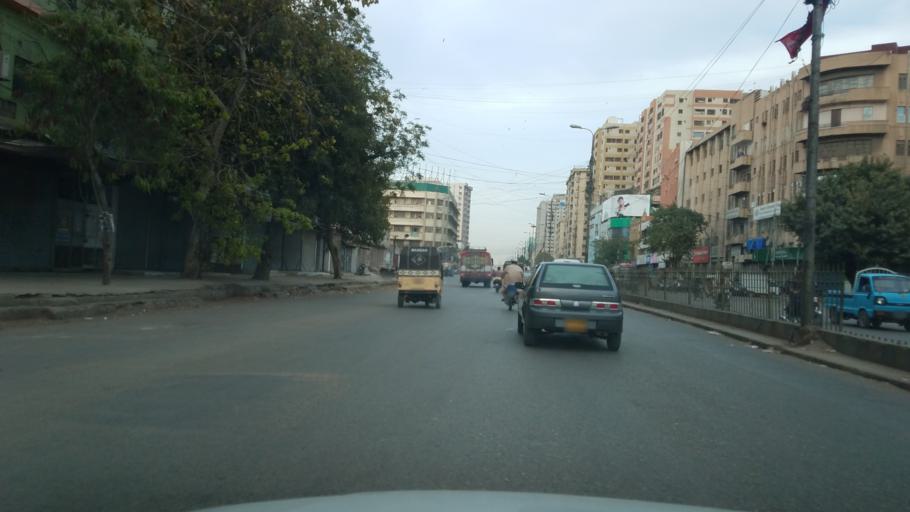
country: PK
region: Sindh
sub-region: Karachi District
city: Karachi
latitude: 24.8643
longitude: 67.0234
